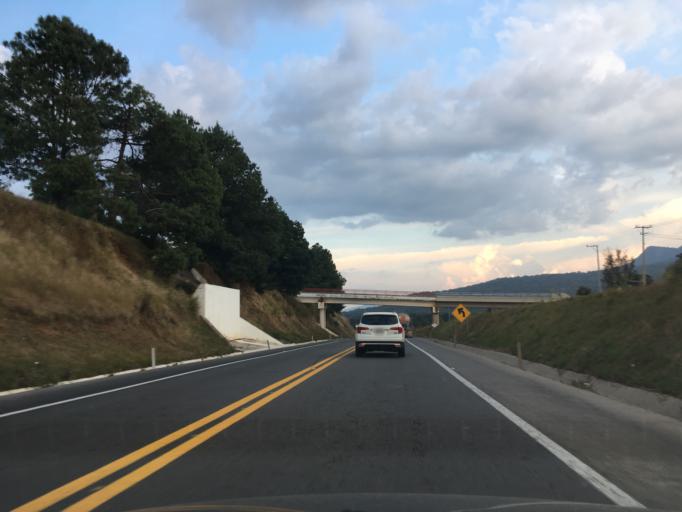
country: MX
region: Michoacan
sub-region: Patzcuaro
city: Colonia Vista Bella (Lomas del Peaje)
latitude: 19.5040
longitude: -101.5796
